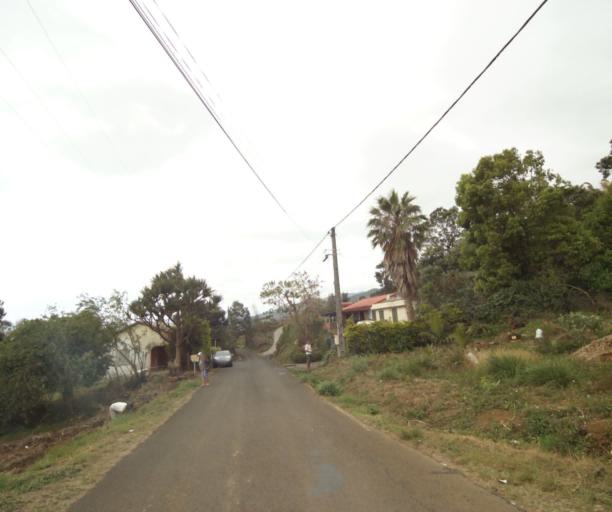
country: RE
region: Reunion
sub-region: Reunion
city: Saint-Paul
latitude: -21.0135
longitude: 55.3360
